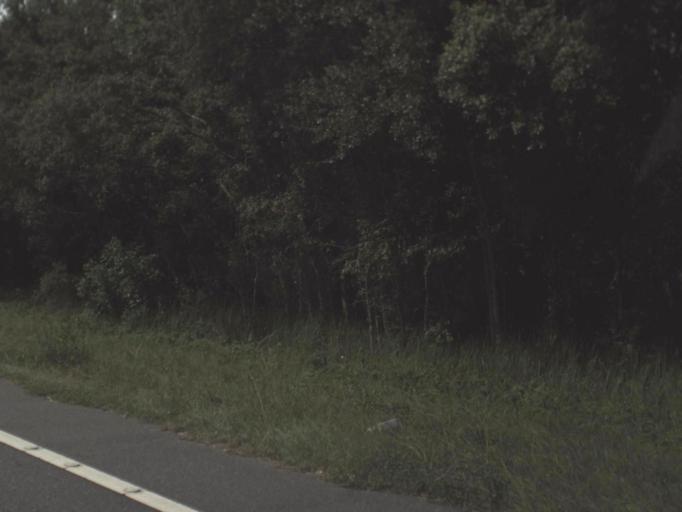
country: US
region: Florida
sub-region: Citrus County
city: Citrus Springs
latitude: 29.0001
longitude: -82.4449
